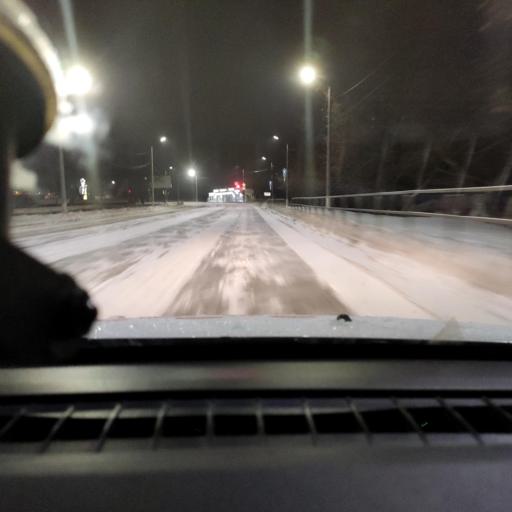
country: RU
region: Samara
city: Novokuybyshevsk
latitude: 53.0919
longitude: 49.9411
